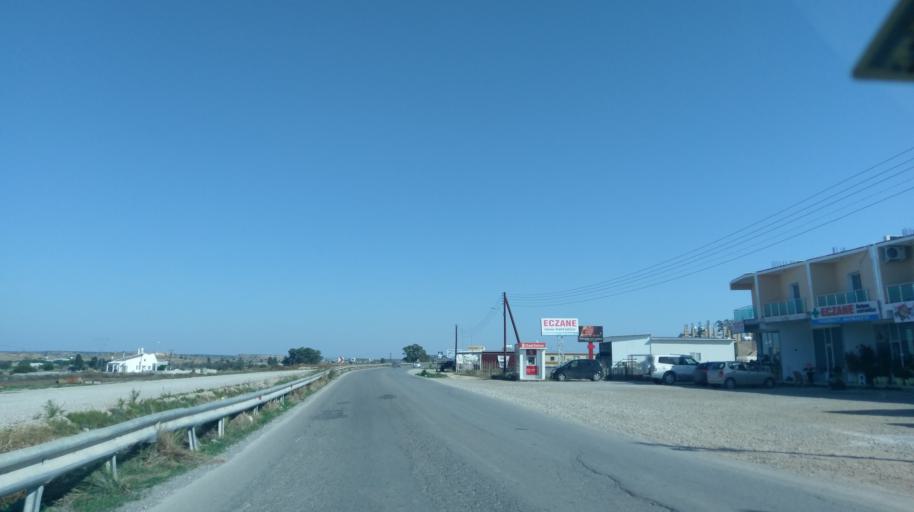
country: CY
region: Ammochostos
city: Leonarisso
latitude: 35.3671
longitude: 34.0236
